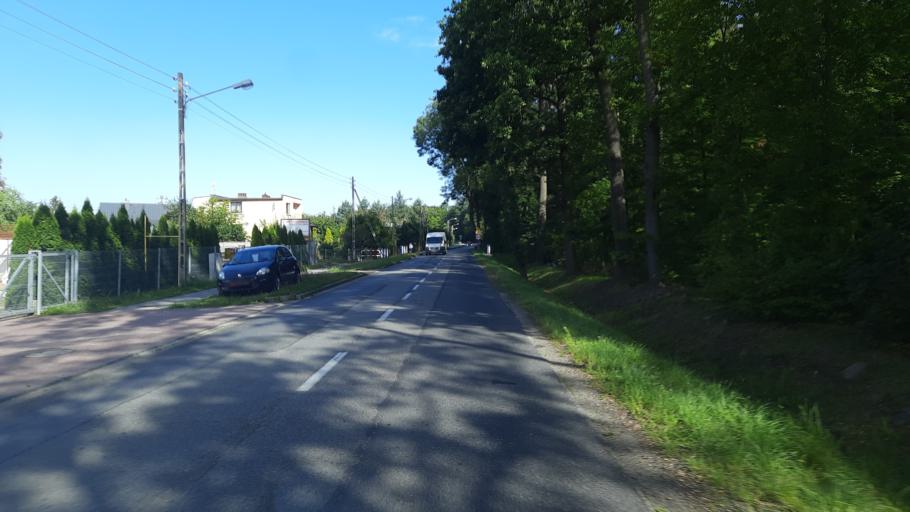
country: PL
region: Lower Silesian Voivodeship
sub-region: Powiat wroclawski
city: Dlugoleka
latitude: 51.1807
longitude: 17.1898
